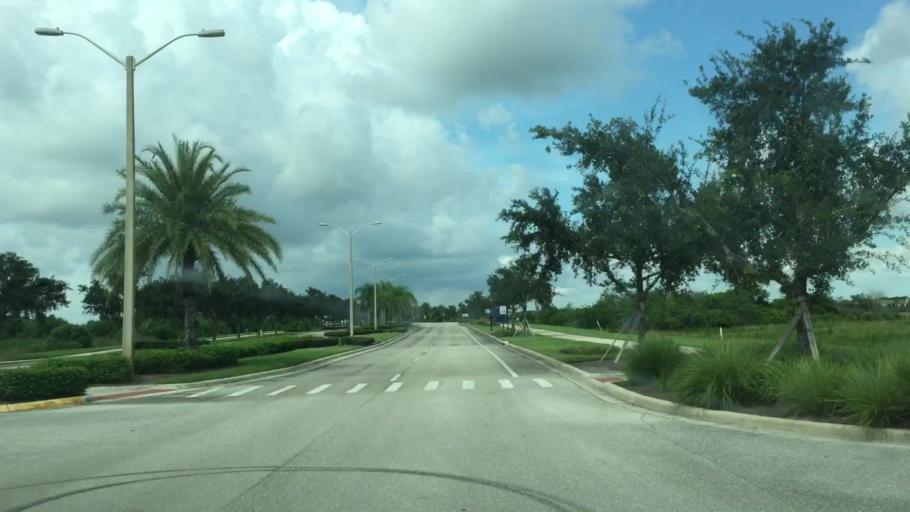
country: US
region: Florida
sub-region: Collier County
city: Immokalee
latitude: 26.3391
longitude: -81.4201
